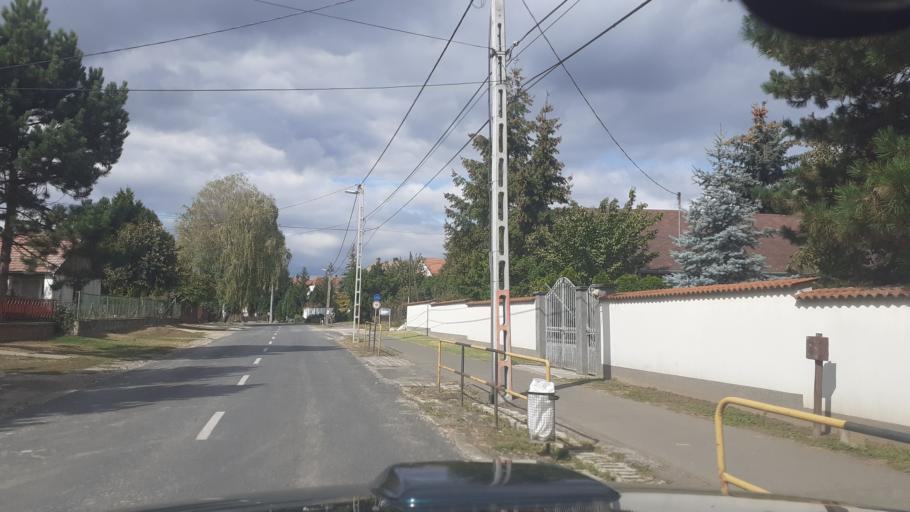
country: HU
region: Bacs-Kiskun
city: Solt
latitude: 46.8113
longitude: 18.9846
